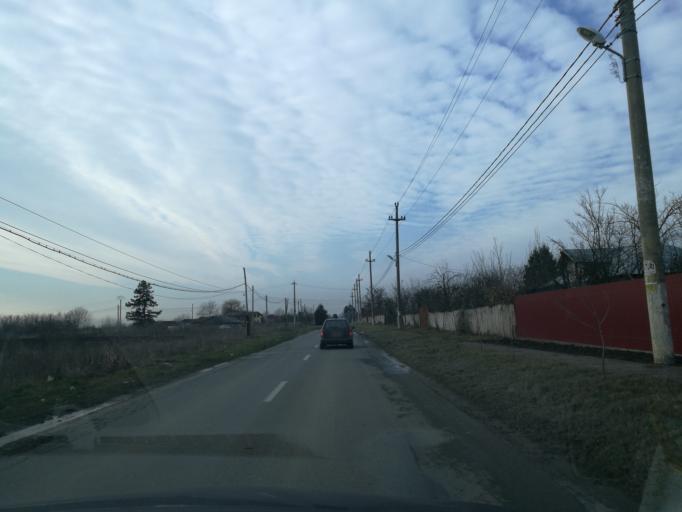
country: RO
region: Ialomita
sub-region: Comuna Fierbinti-Targ
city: Fierbinti-Targ
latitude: 44.6790
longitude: 26.3655
